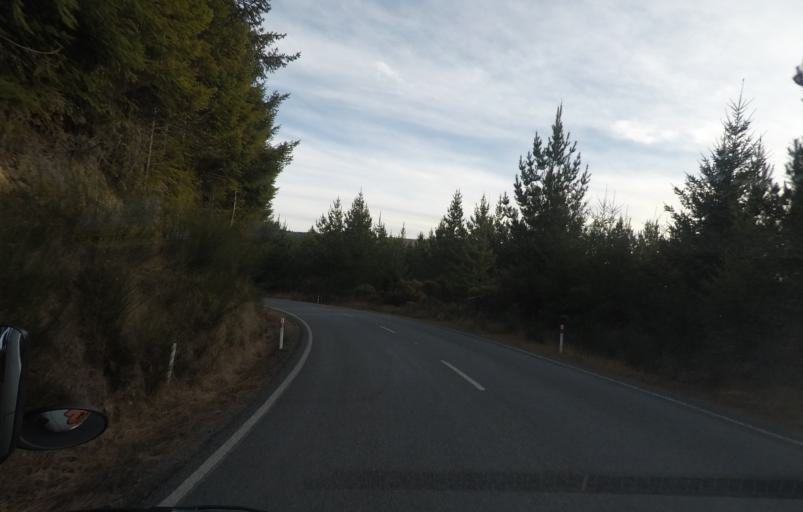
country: NZ
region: Tasman
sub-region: Tasman District
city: Wakefield
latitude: -41.6616
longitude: 172.8752
